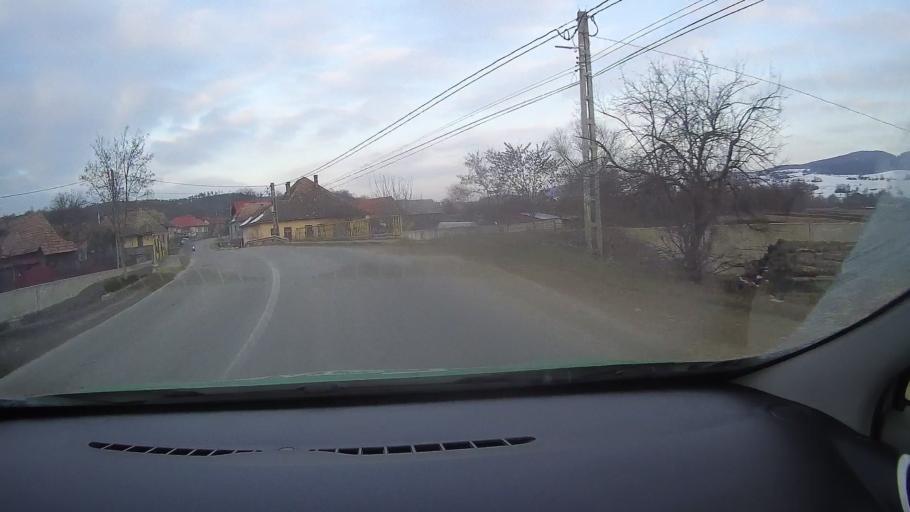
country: RO
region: Harghita
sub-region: Comuna Simonesti
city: Simonesti
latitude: 46.3568
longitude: 25.1473
